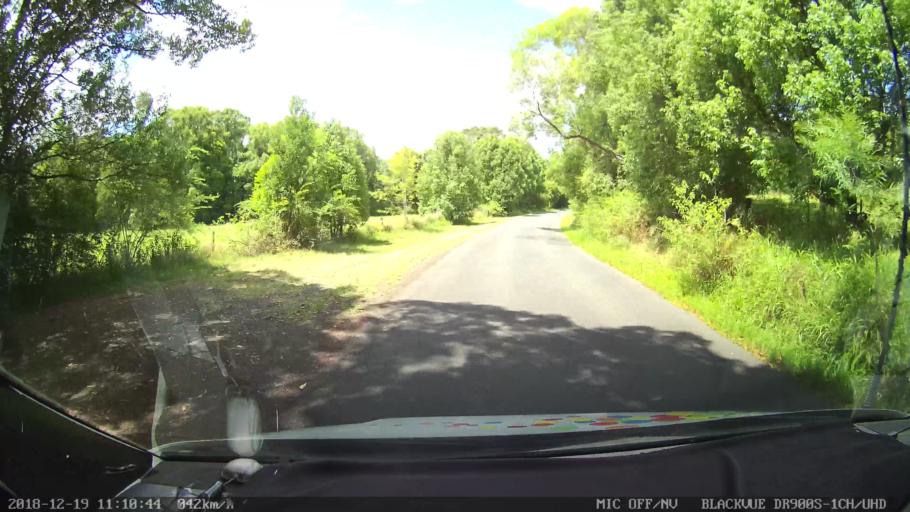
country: AU
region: New South Wales
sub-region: Lismore Municipality
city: Nimbin
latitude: -28.6397
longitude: 153.2599
